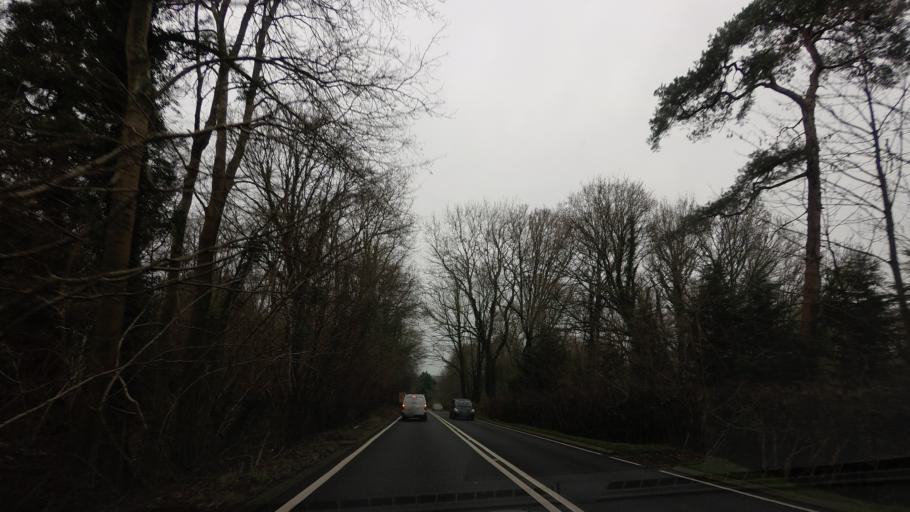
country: GB
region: England
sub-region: East Sussex
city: Saint Leonards-on-Sea
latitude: 50.8994
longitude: 0.5547
